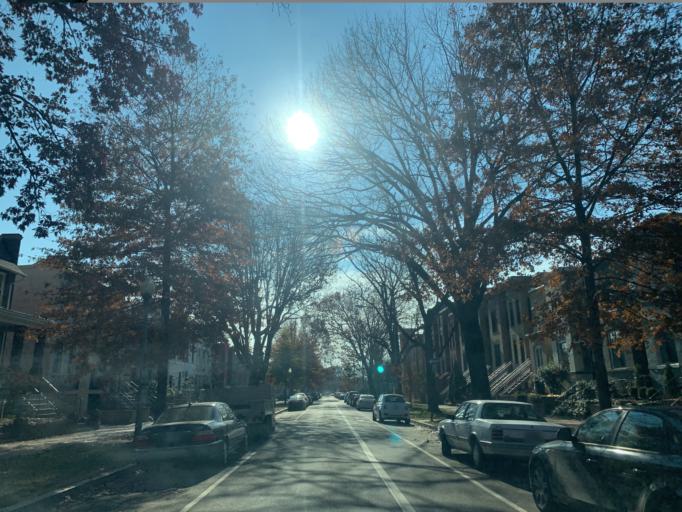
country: US
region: Washington, D.C.
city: Washington, D.C.
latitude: 38.8865
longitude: -76.9855
